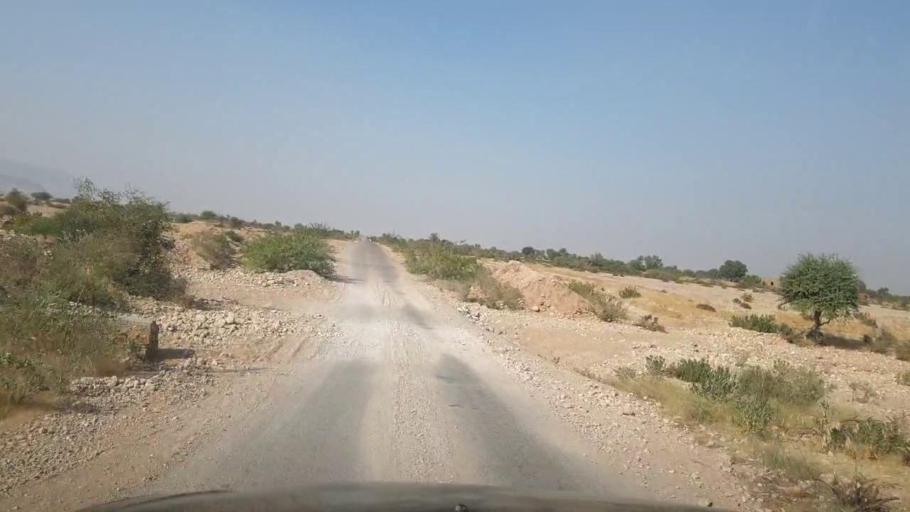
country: PK
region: Sindh
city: Jamshoro
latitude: 25.5856
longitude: 67.8201
